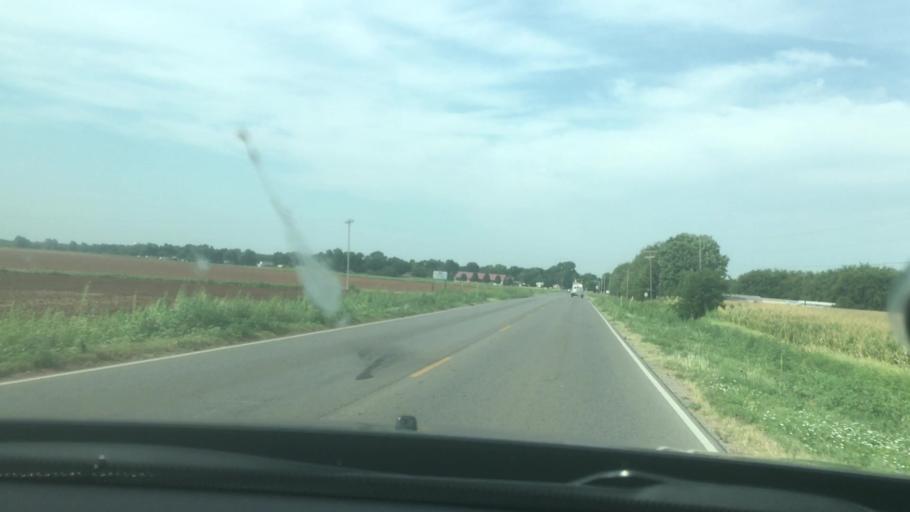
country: US
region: Oklahoma
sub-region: Garvin County
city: Pauls Valley
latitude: 34.7544
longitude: -97.2048
